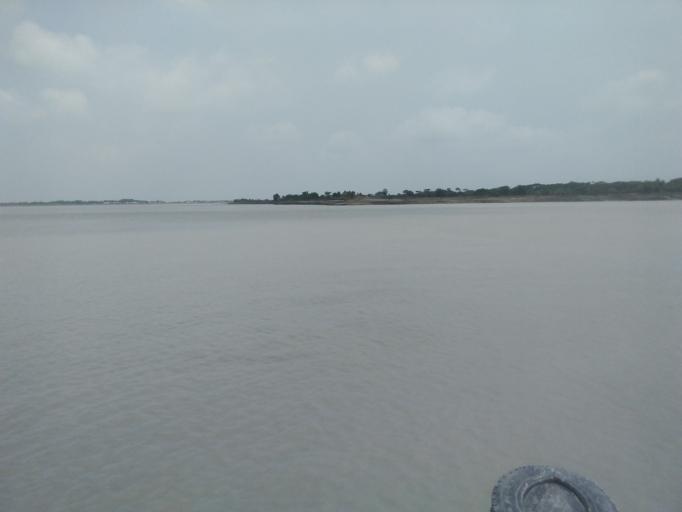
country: BD
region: Khulna
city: Phultala
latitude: 22.6433
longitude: 89.4124
